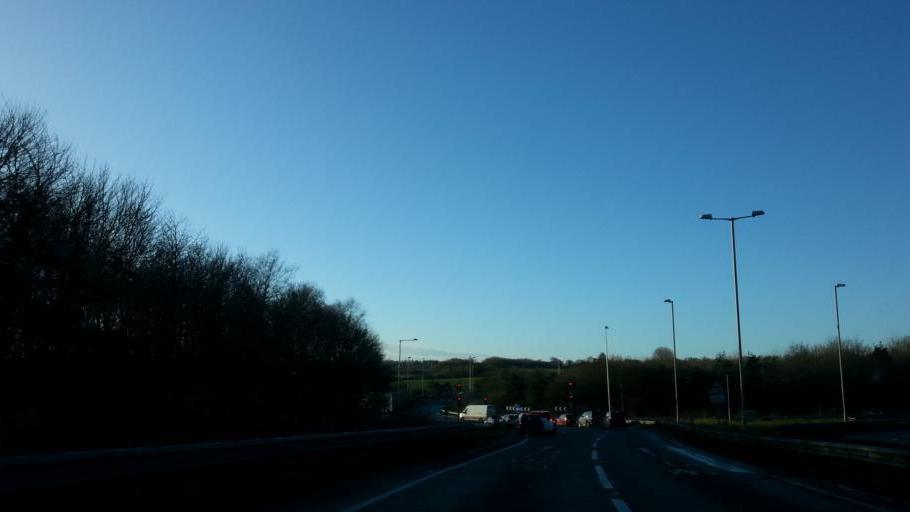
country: GB
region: England
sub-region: Suffolk
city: Bramford
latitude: 52.0372
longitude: 1.1006
